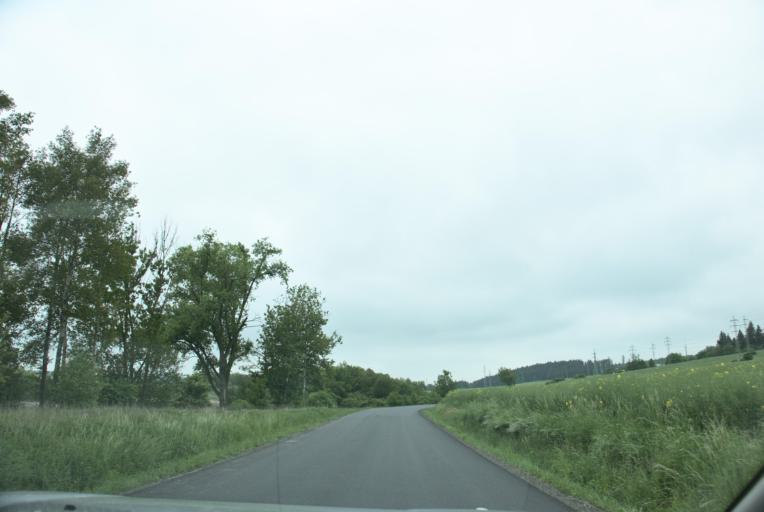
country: CZ
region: Plzensky
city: Kralovice
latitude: 49.9863
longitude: 13.4652
